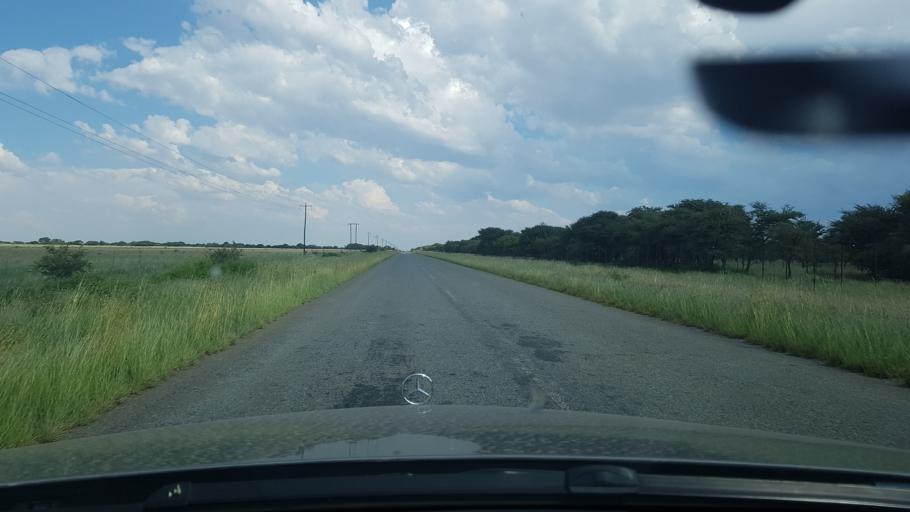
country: ZA
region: North-West
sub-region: Dr Ruth Segomotsi Mompati District Municipality
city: Bloemhof
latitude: -27.7510
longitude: 25.5927
